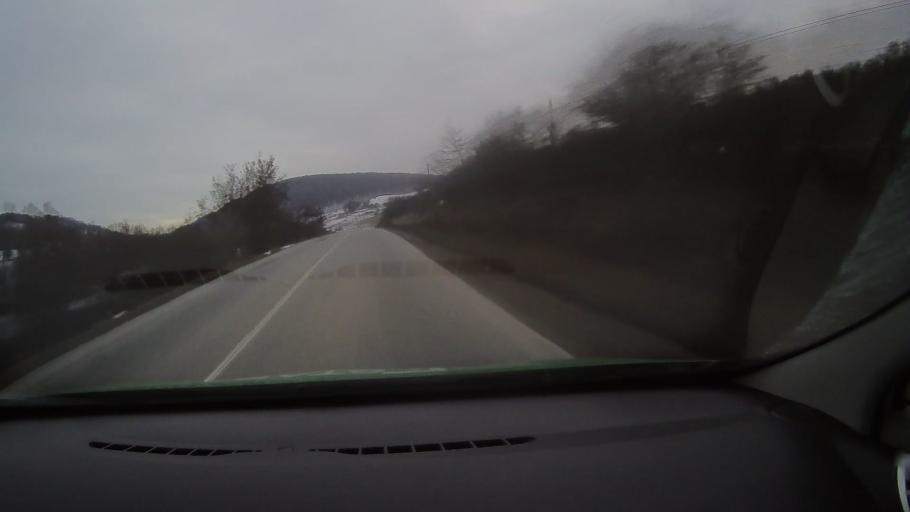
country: RO
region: Harghita
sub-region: Comuna Mugeni
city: Mugeni
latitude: 46.2323
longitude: 25.2421
